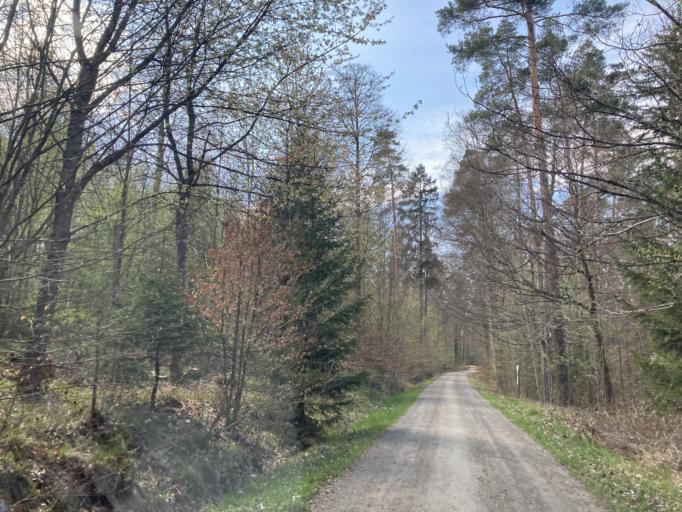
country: DE
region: Baden-Wuerttemberg
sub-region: Tuebingen Region
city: Dettenhausen
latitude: 48.5979
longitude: 9.1188
